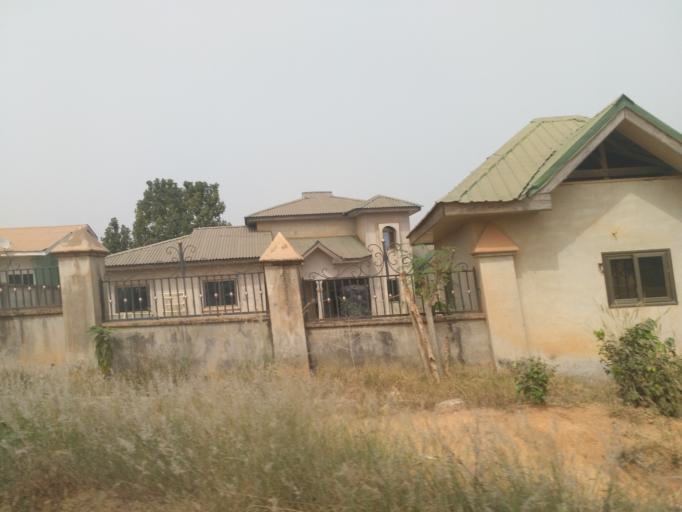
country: GH
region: Ashanti
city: Mamponteng
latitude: 6.6656
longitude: -1.5447
